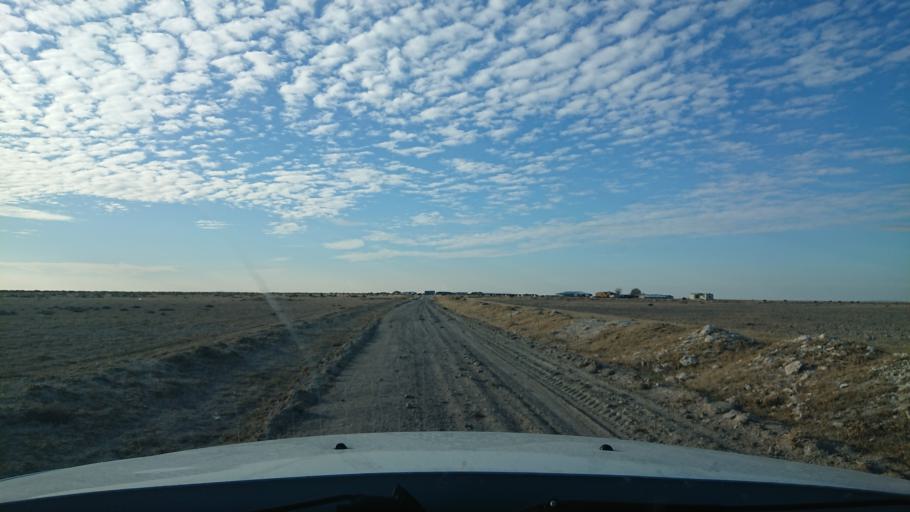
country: TR
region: Aksaray
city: Eskil
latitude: 38.5657
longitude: 33.3008
